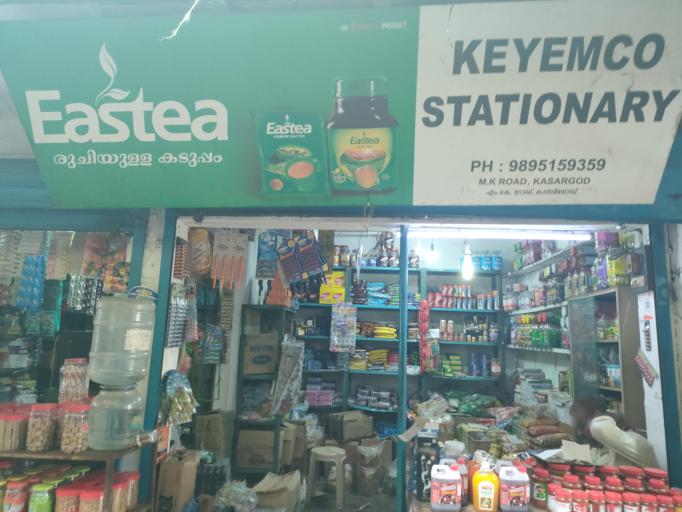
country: IN
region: Kerala
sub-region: Kasaragod District
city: Kasaragod
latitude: 12.4998
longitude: 74.9891
